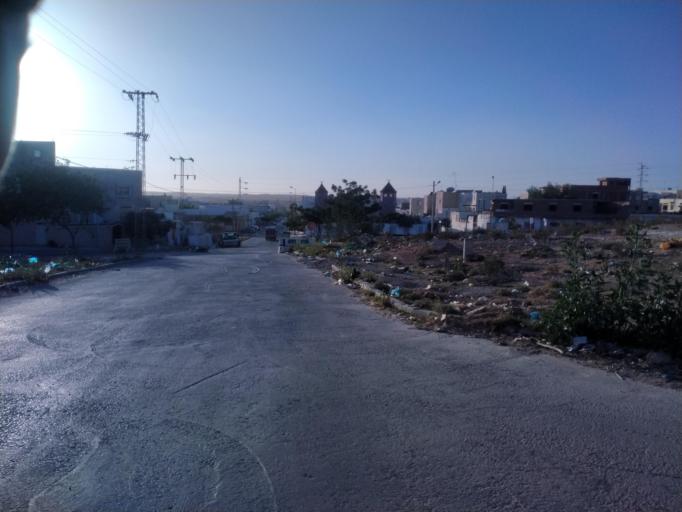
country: TN
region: Susah
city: Akouda
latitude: 35.8171
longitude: 10.5543
